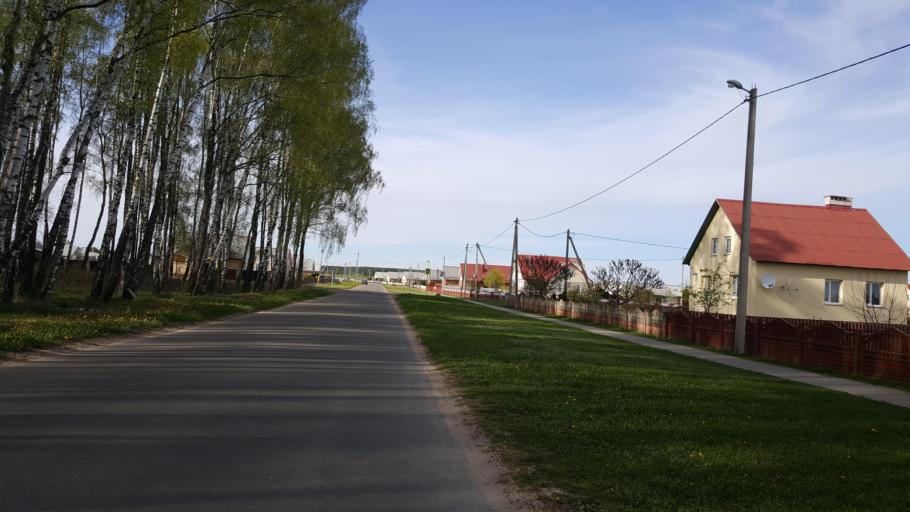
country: BY
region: Brest
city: Vysokaye
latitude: 52.4090
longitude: 23.4606
